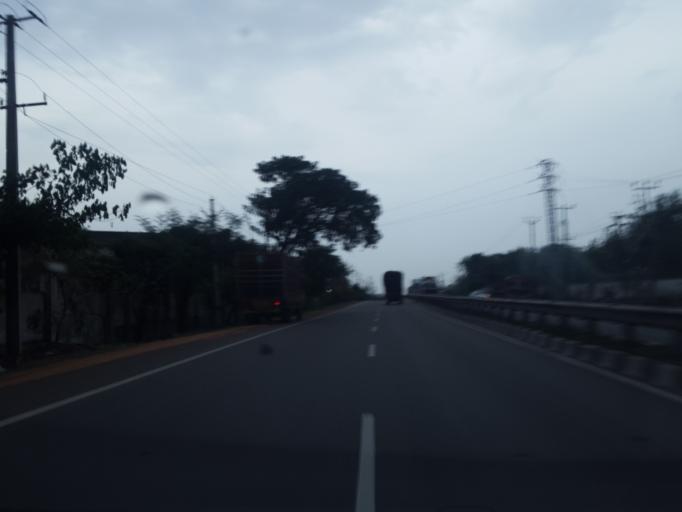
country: IN
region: Telangana
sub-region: Rangareddi
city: Sriramnagar
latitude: 17.1592
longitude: 78.2948
